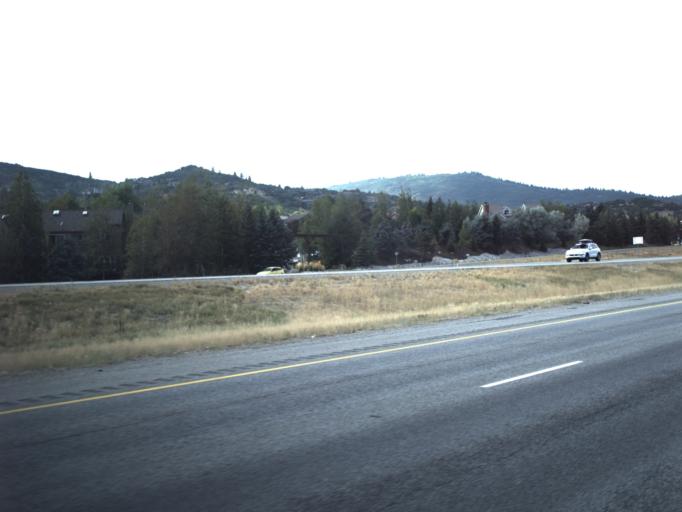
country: US
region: Utah
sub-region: Summit County
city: Summit Park
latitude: 40.7469
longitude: -111.5647
